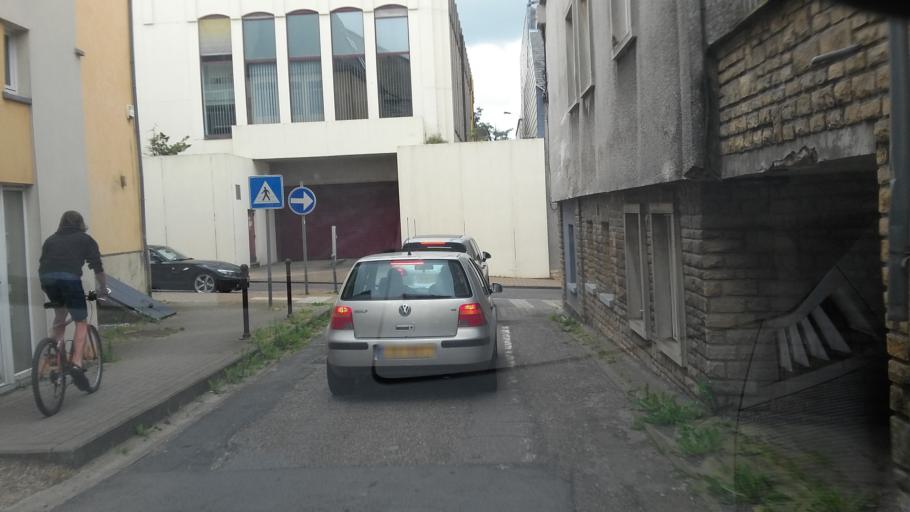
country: BE
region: Wallonia
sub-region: Province du Luxembourg
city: Arlon
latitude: 49.6828
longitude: 5.8162
